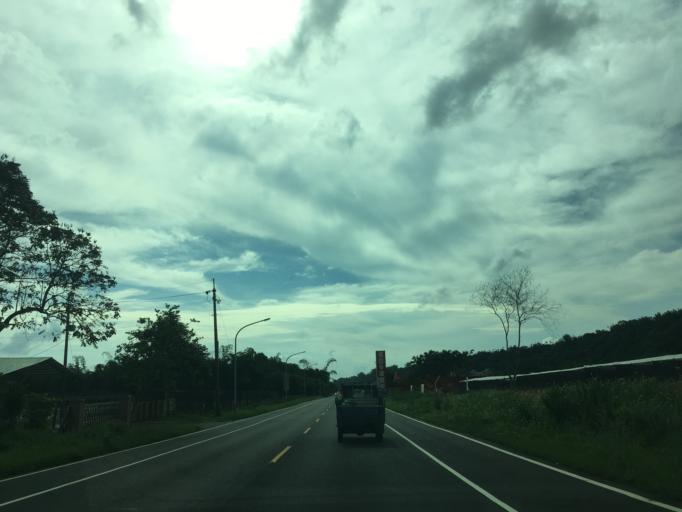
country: TW
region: Taiwan
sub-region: Chiayi
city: Jiayi Shi
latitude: 23.4475
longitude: 120.5793
